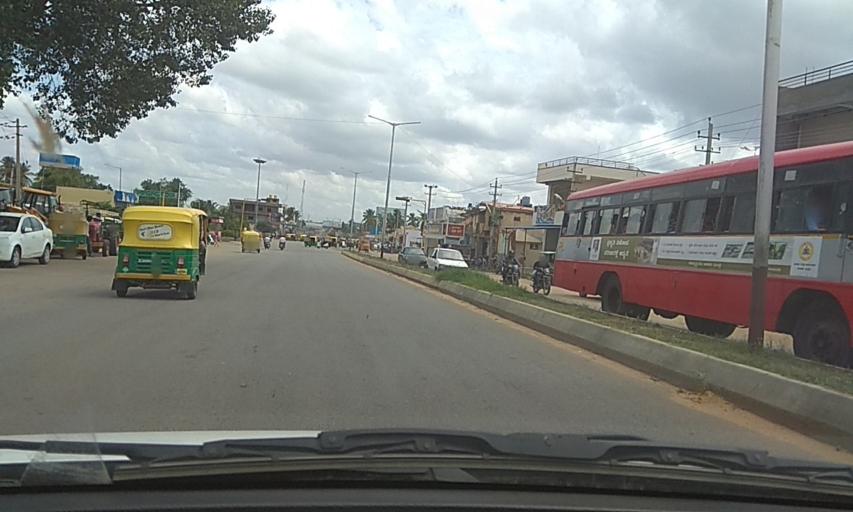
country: IN
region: Karnataka
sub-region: Tumkur
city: Tumkur
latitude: 13.3642
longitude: 77.1033
